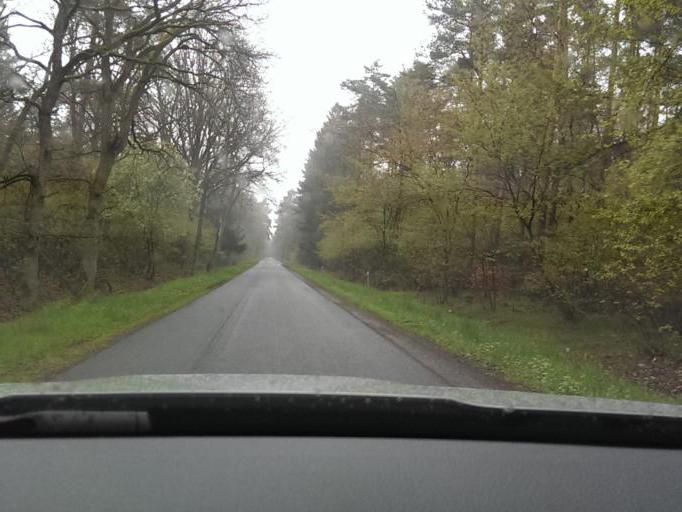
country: DE
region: Lower Saxony
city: Elze
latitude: 52.5999
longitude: 9.7755
